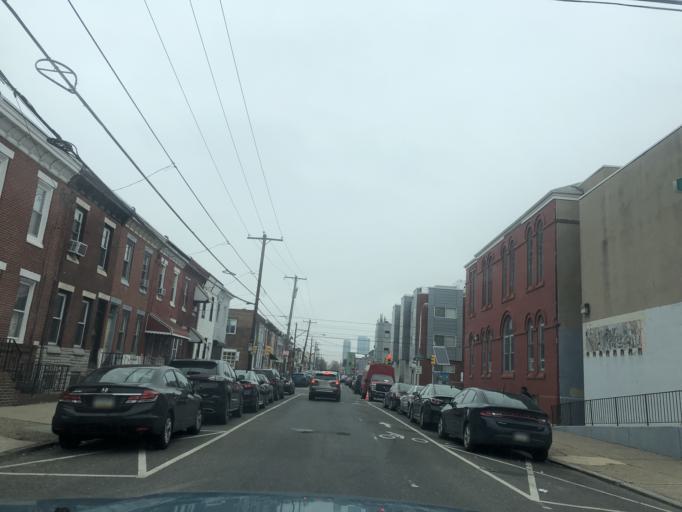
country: US
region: Pennsylvania
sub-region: Philadelphia County
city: Philadelphia
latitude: 39.9374
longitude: -75.1802
